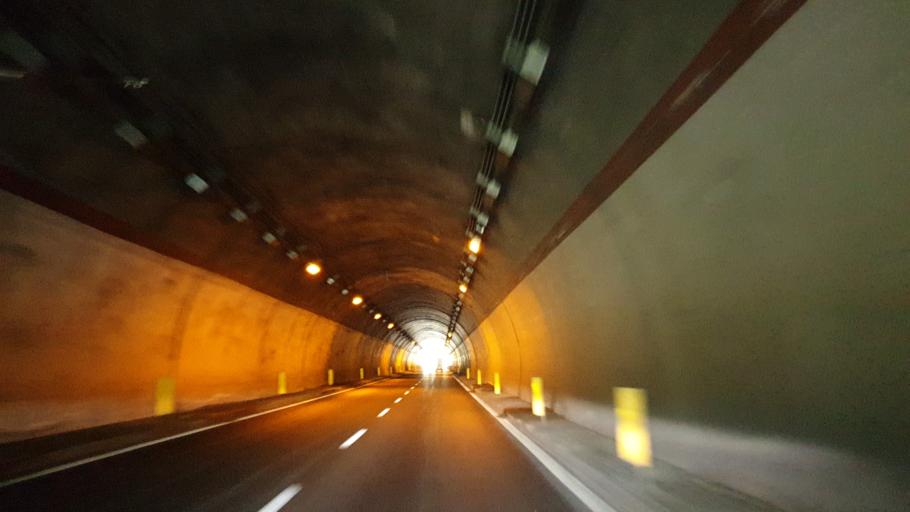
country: IT
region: Emilia-Romagna
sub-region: Forli-Cesena
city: Sarsina
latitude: 43.9182
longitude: 12.1457
